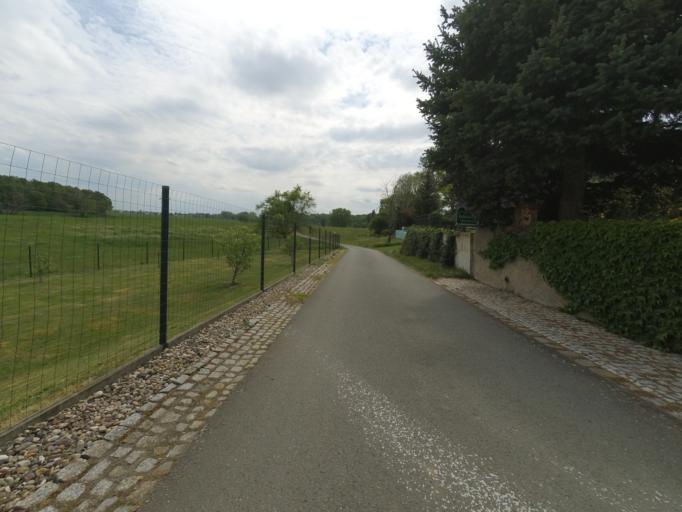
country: DE
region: Saxony
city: Strehla
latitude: 51.3681
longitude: 13.2308
